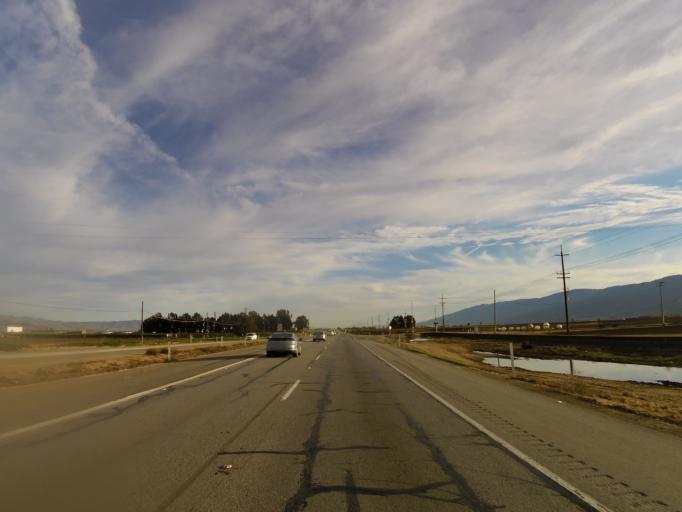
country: US
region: California
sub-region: Monterey County
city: Chualar
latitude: 36.5970
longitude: -121.5471
